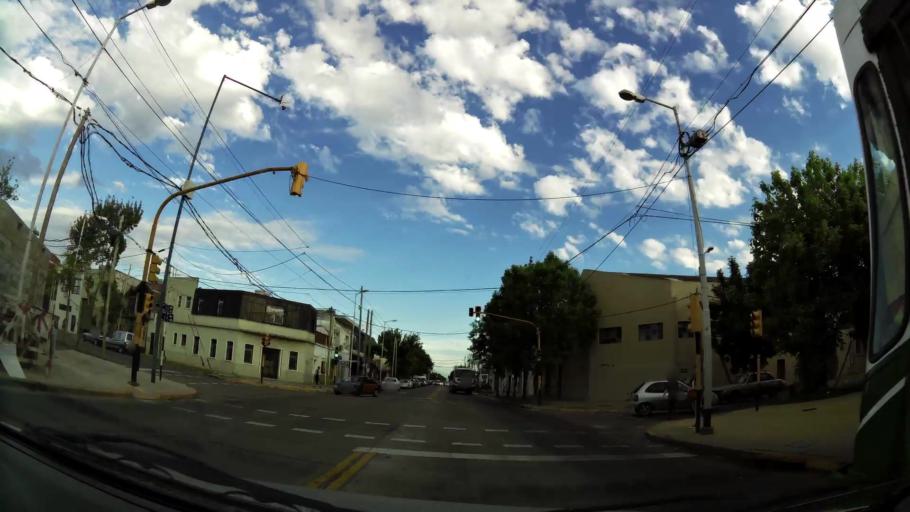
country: AR
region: Buenos Aires
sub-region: Partido de Avellaneda
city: Avellaneda
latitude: -34.6776
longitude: -58.3548
